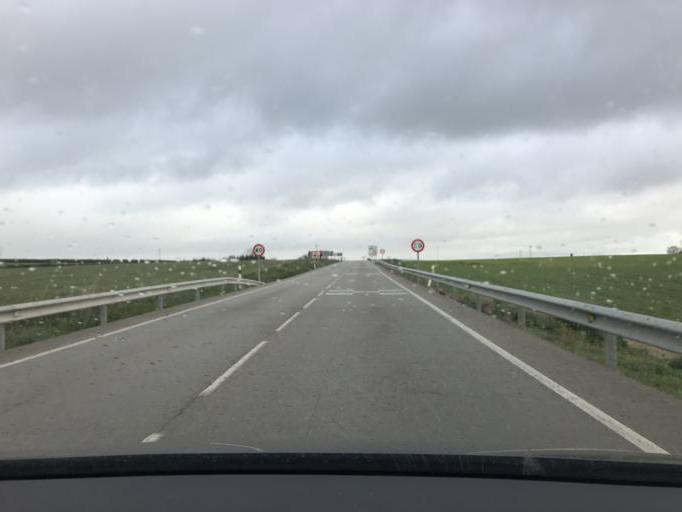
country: ES
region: Andalusia
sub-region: Provincia de Sevilla
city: La Lantejuela
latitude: 37.3900
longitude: -5.3020
